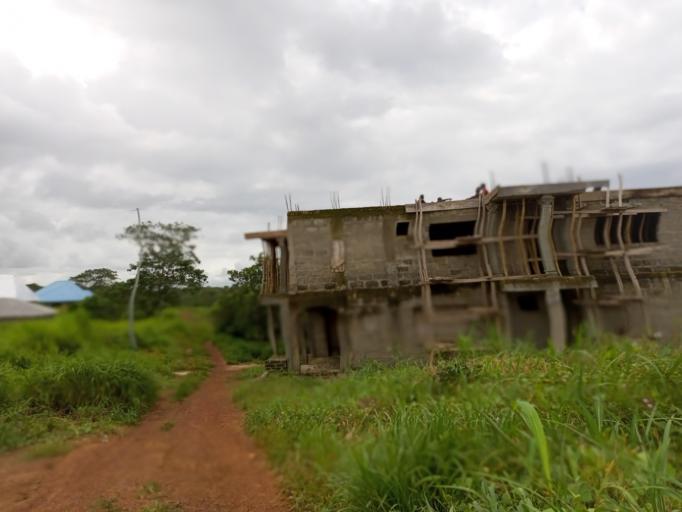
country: SL
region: Northern Province
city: Kamakwie
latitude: 9.5008
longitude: -12.2502
